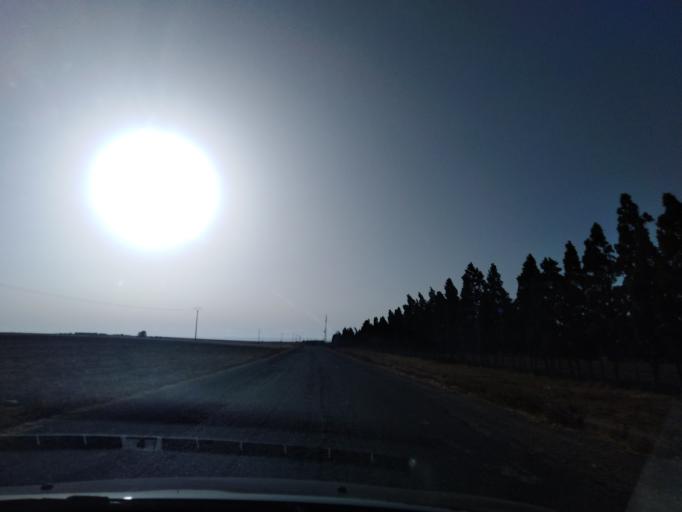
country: MA
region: Doukkala-Abda
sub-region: Safi
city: Safi
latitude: 32.4841
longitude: -8.9130
